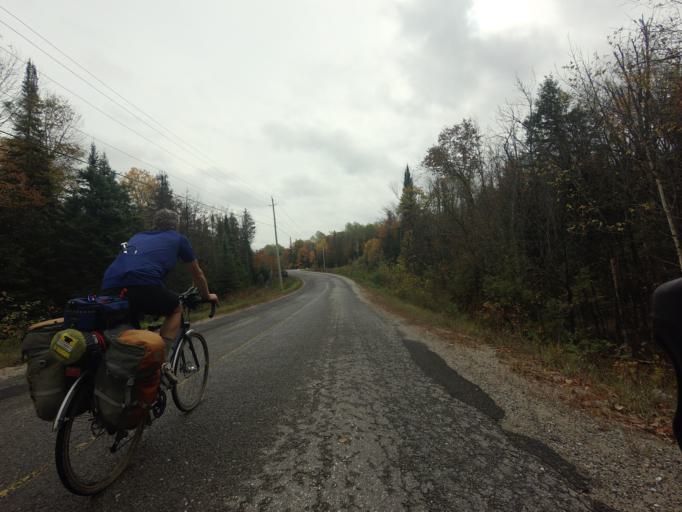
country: CA
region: Ontario
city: Perth
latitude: 45.1155
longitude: -76.5125
